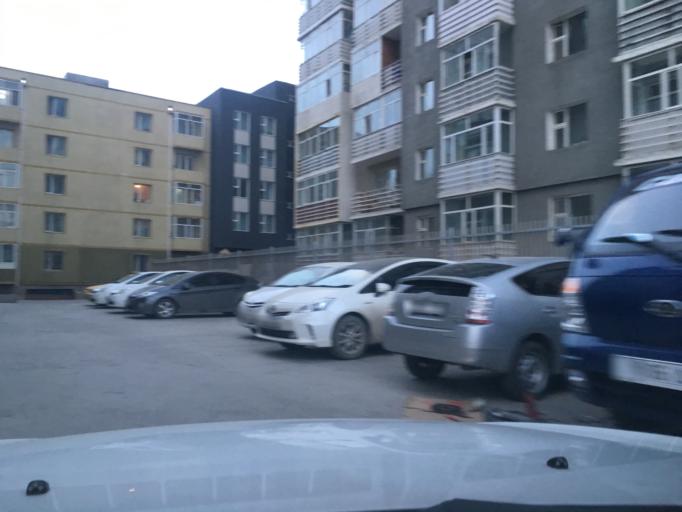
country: MN
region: Ulaanbaatar
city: Ulaanbaatar
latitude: 47.9118
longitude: 106.8643
